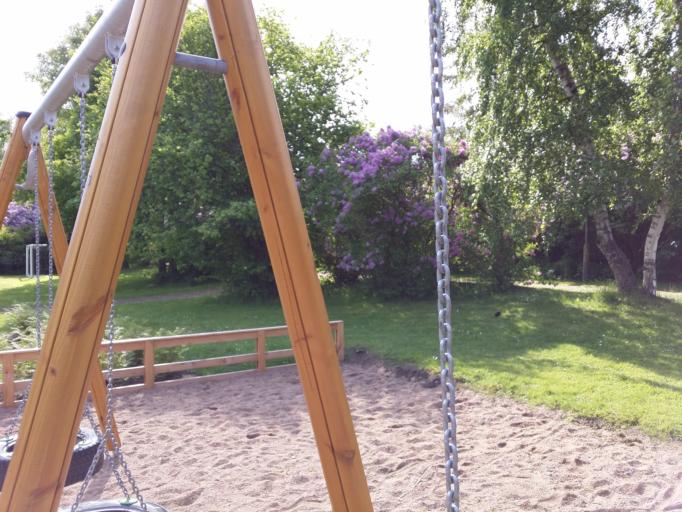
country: SE
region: Skane
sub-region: Burlovs Kommun
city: Arloev
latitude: 55.5976
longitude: 13.0852
